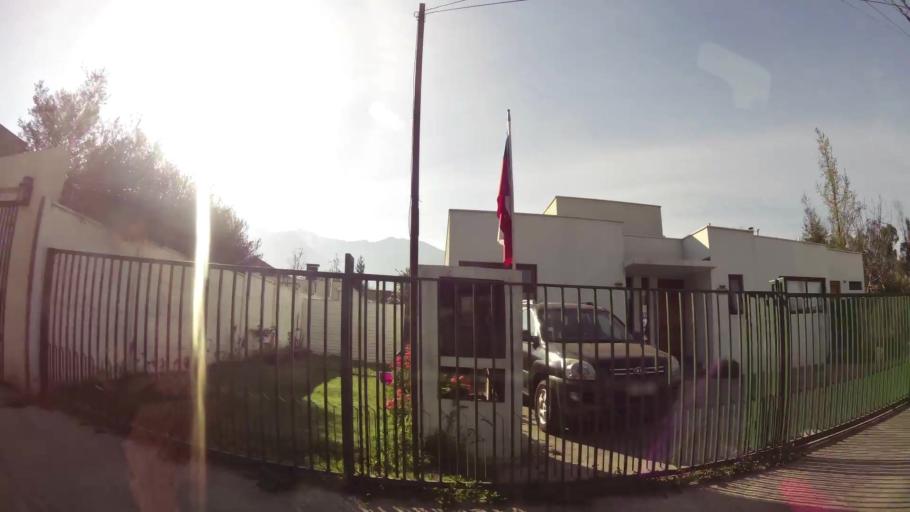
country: CL
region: Santiago Metropolitan
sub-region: Provincia de Santiago
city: Villa Presidente Frei, Nunoa, Santiago, Chile
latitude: -33.4945
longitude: -70.5493
